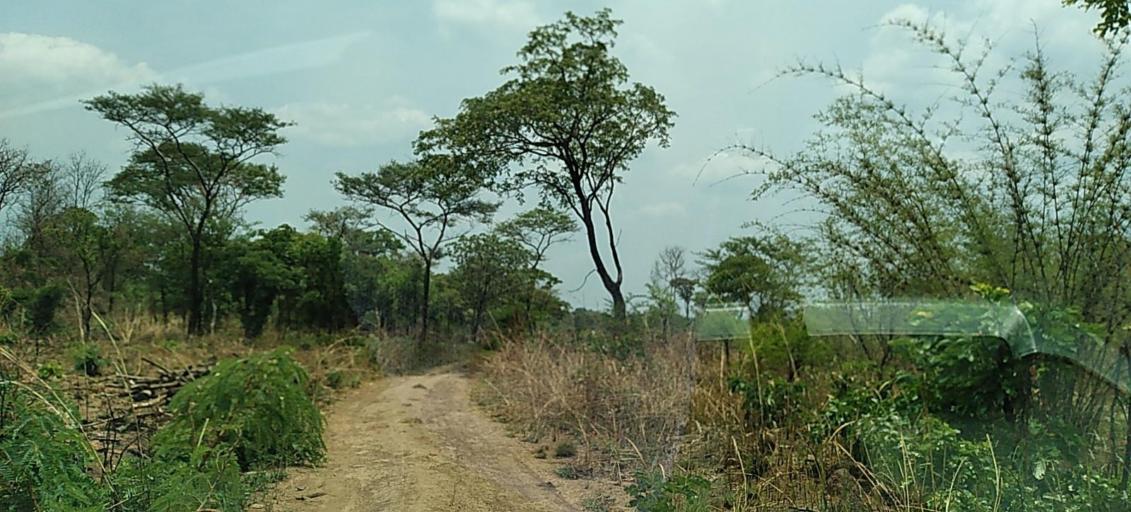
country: ZM
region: Copperbelt
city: Chililabombwe
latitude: -12.3784
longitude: 27.6439
